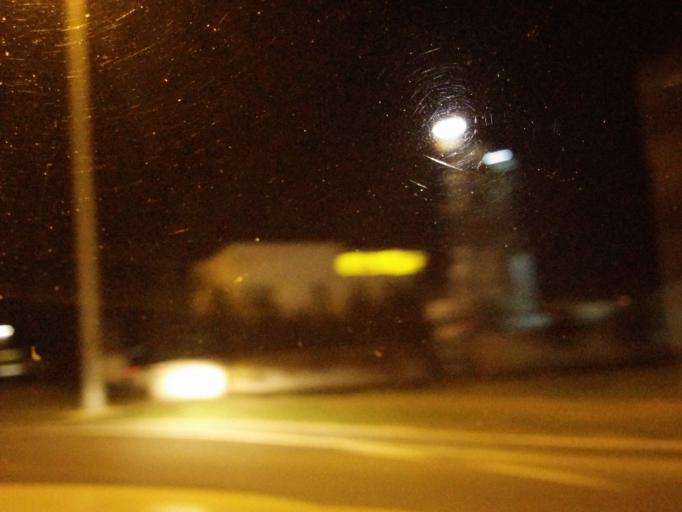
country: HR
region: Brodsko-Posavska
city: Bukovlje
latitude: 45.1753
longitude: 18.0627
